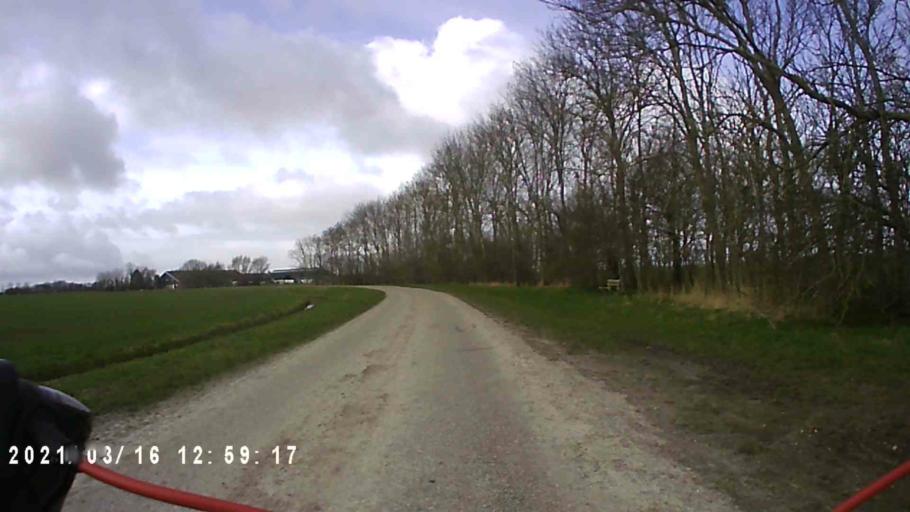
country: NL
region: Friesland
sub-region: Menameradiel
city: Berltsum
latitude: 53.2549
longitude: 5.6510
